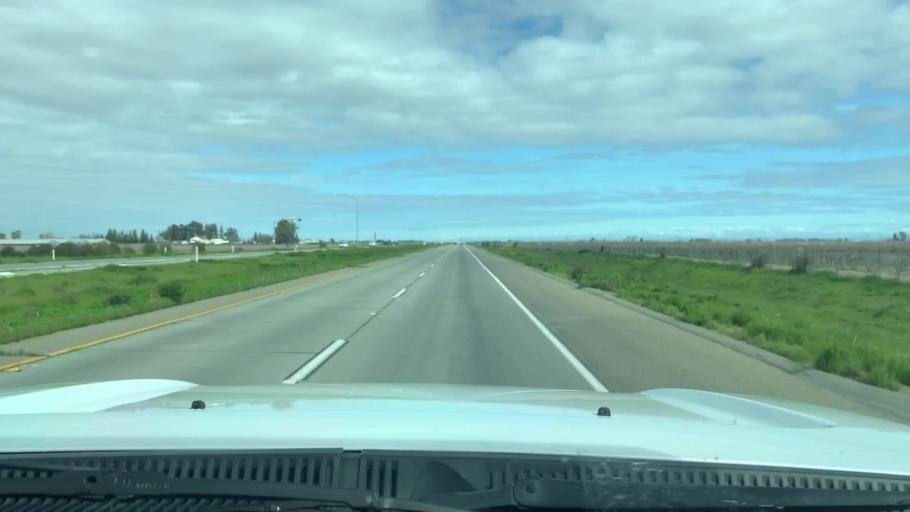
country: US
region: California
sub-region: Fresno County
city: Caruthers
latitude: 36.5484
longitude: -119.7860
